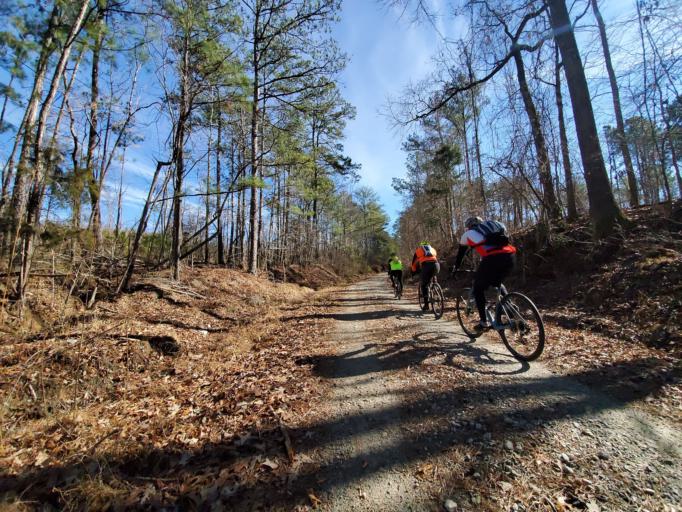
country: US
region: Georgia
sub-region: Fulton County
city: Chattahoochee Hills
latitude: 33.5701
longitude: -84.7584
